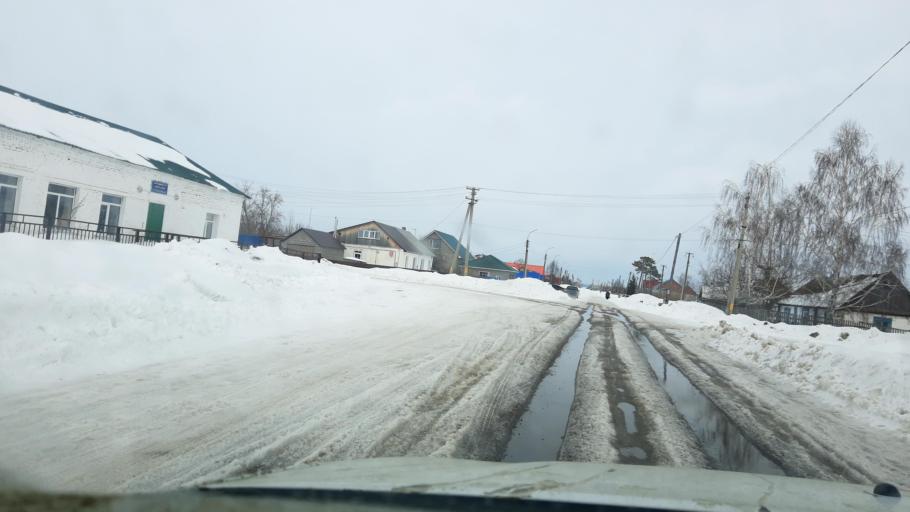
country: RU
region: Bashkortostan
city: Karmaskaly
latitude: 54.4142
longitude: 56.1601
